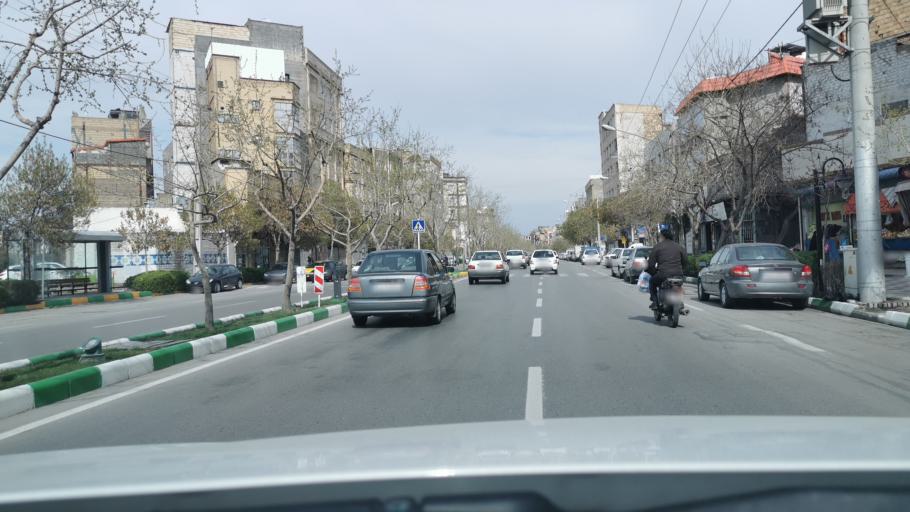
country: IR
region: Razavi Khorasan
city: Mashhad
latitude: 36.3161
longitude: 59.5970
